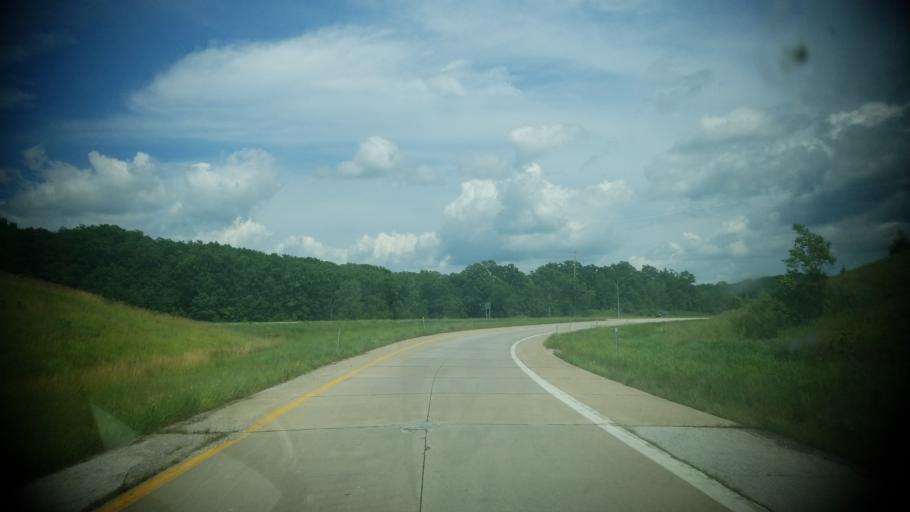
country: US
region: Missouri
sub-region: Pike County
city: Bowling Green
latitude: 39.3575
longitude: -91.2026
